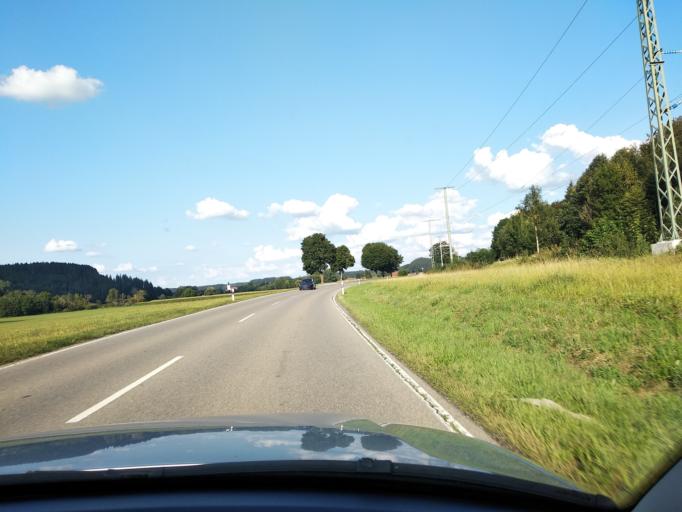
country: DE
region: Baden-Wuerttemberg
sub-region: Tuebingen Region
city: Aichstetten
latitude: 47.8860
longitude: 10.0575
